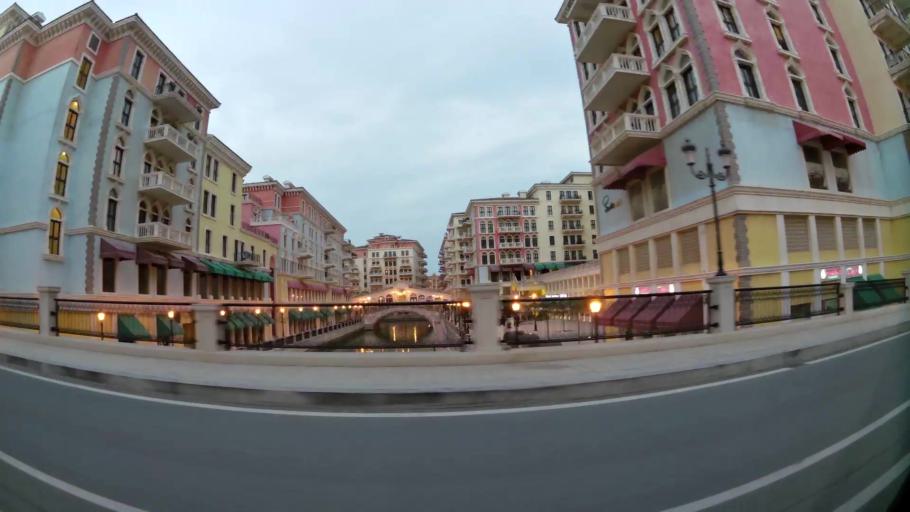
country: QA
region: Baladiyat ad Dawhah
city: Doha
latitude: 25.3761
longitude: 51.5436
